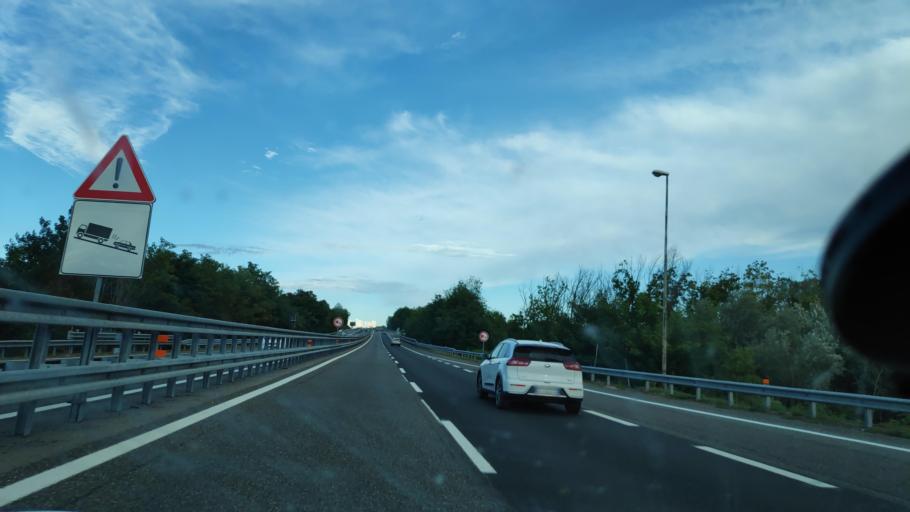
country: IT
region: Piedmont
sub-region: Provincia di Asti
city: Cerro Tanaro
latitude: 44.9047
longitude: 8.3677
